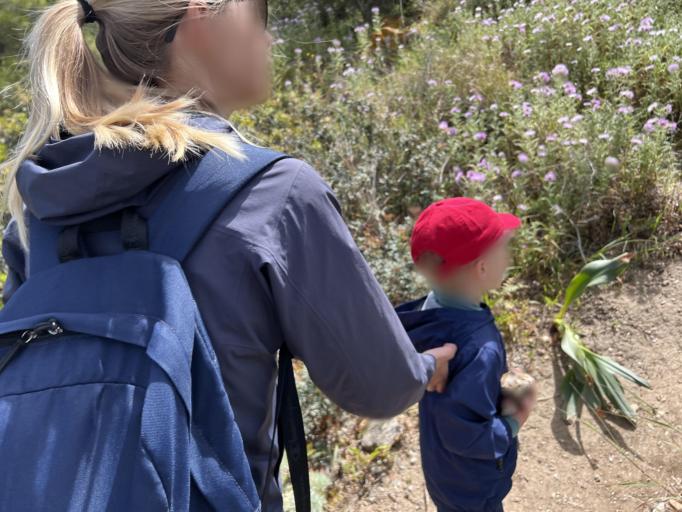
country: IT
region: Sardinia
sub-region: Provincia di Cagliari
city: Domus de Maria
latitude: 38.8959
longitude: 8.8840
